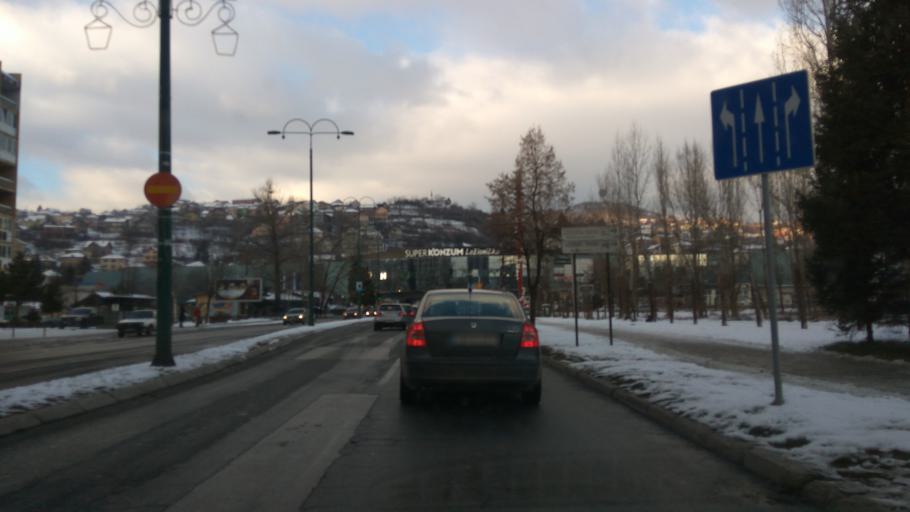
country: BA
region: Federation of Bosnia and Herzegovina
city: Kobilja Glava
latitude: 43.8553
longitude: 18.3847
